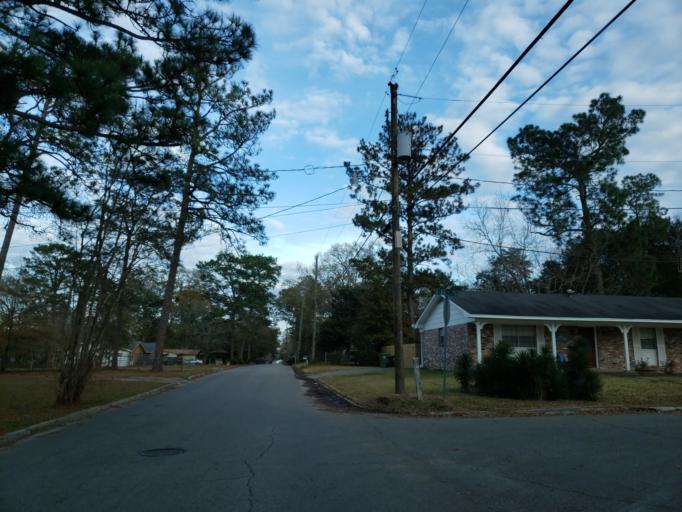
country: US
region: Mississippi
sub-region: Forrest County
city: Hattiesburg
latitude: 31.3028
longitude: -89.3295
